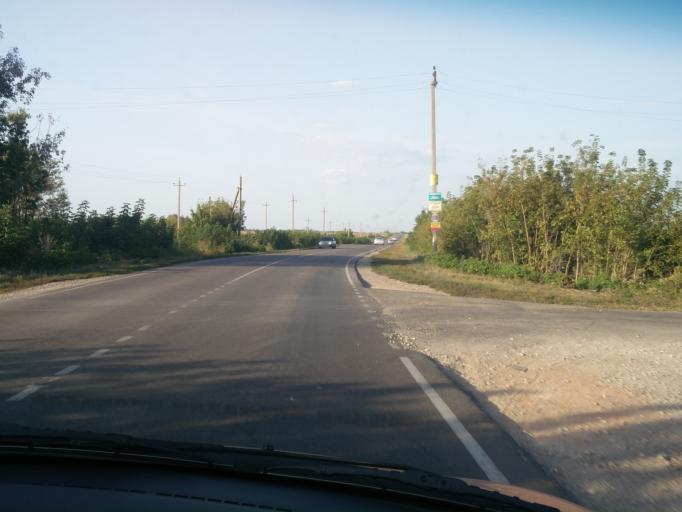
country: RU
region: Voronezj
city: Ramon'
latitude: 51.9239
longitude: 39.3235
